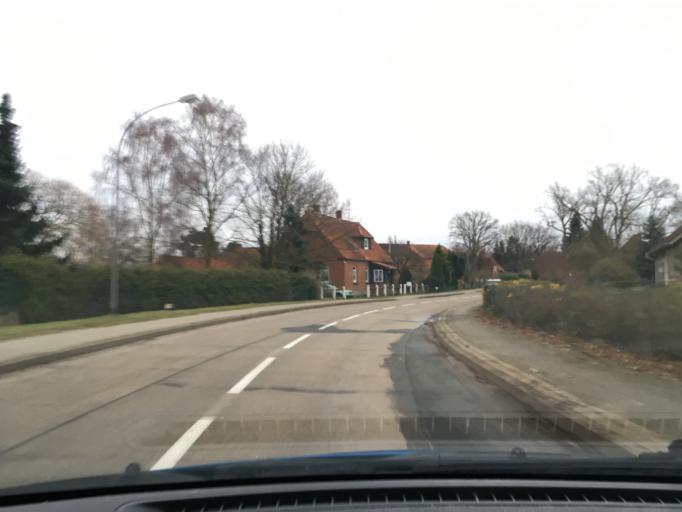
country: DE
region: Lower Saxony
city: Bleckede
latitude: 53.2837
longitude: 10.7529
